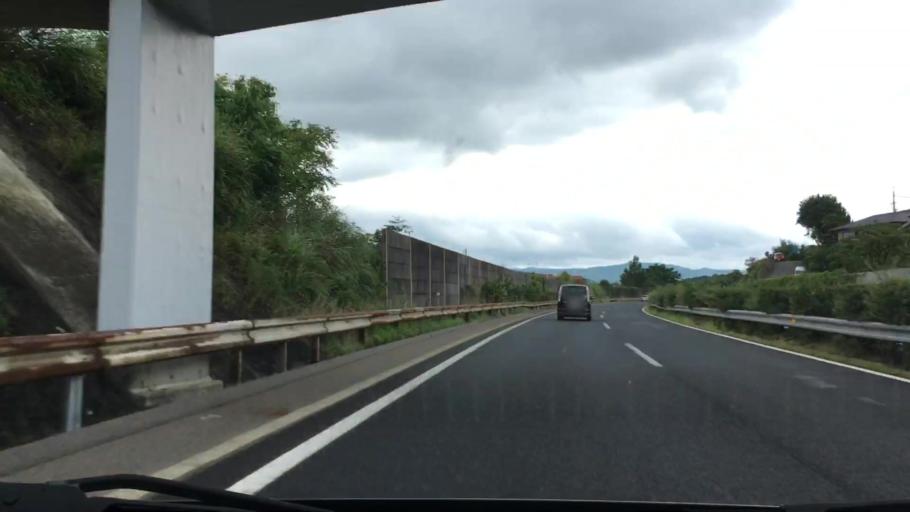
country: JP
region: Okayama
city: Tsuyama
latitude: 35.0642
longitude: 133.9830
